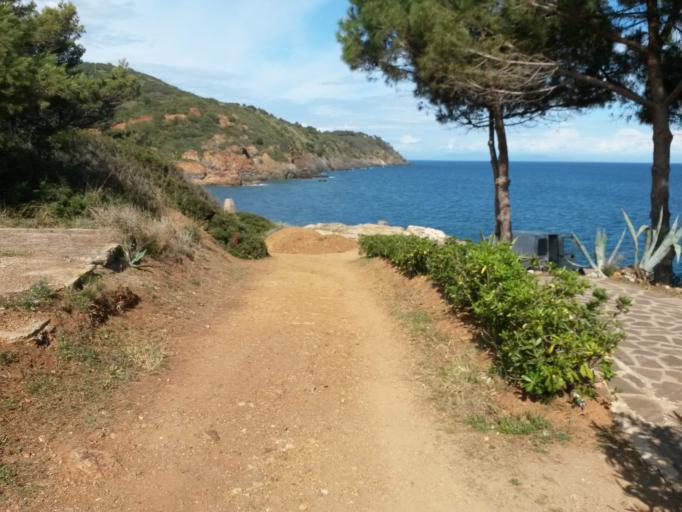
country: IT
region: Tuscany
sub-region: Provincia di Livorno
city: Porto Azzurro
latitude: 42.7716
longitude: 10.4178
